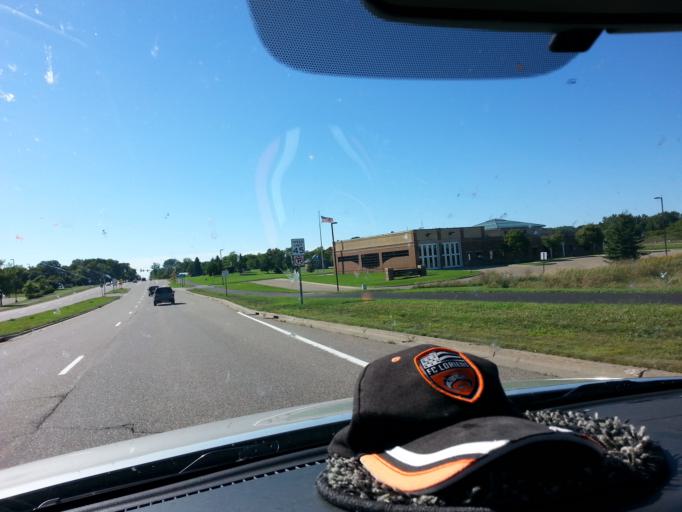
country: US
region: Minnesota
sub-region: Dakota County
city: Lakeville
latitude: 44.6814
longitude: -93.2535
